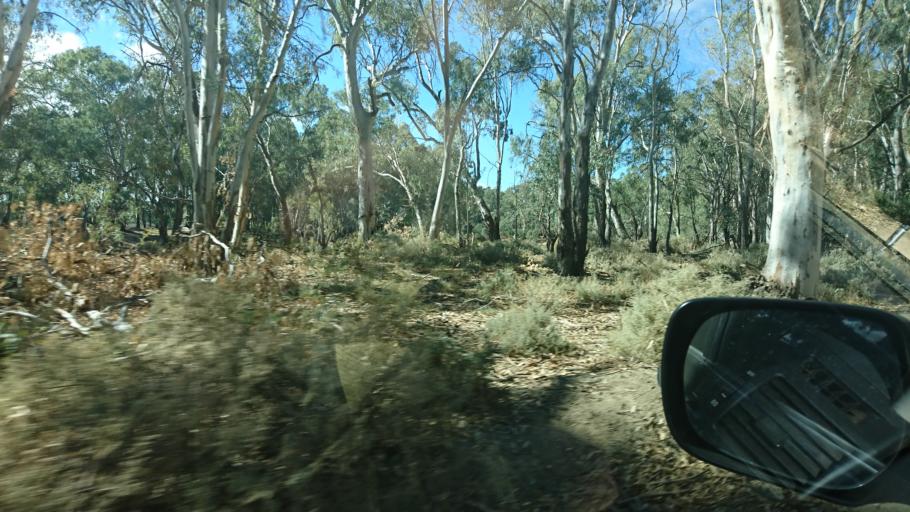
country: AU
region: Victoria
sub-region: Swan Hill
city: Swan Hill
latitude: -35.1423
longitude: 143.3861
